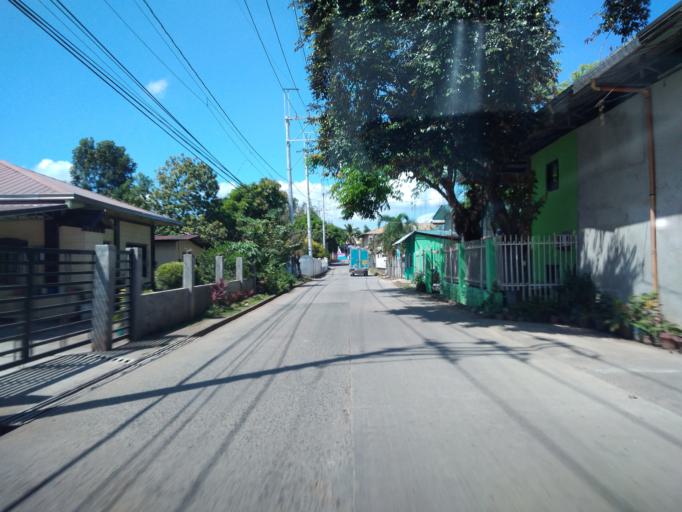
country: PH
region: Central Luzon
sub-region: Province of Bulacan
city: Bitungol
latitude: 14.8596
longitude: 121.0377
